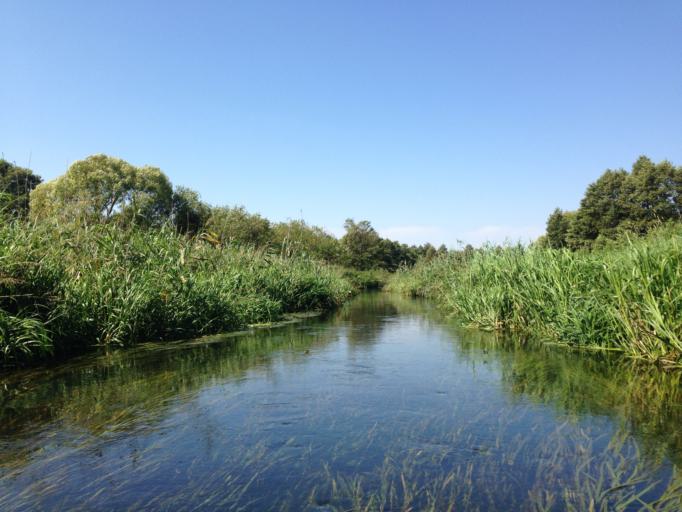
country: PL
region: Kujawsko-Pomorskie
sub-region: Powiat brodnicki
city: Bartniczka
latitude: 53.2806
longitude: 19.5804
